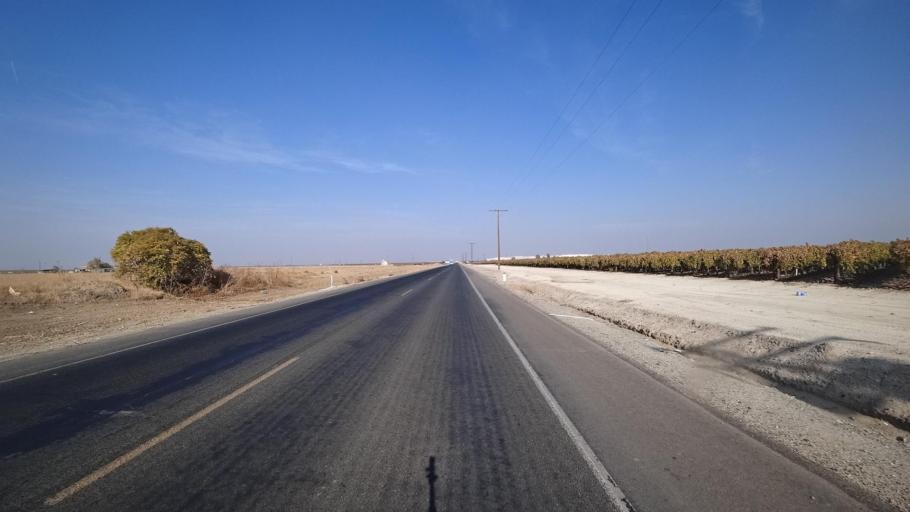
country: US
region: California
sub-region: Kern County
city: McFarland
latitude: 35.7145
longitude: -119.1620
